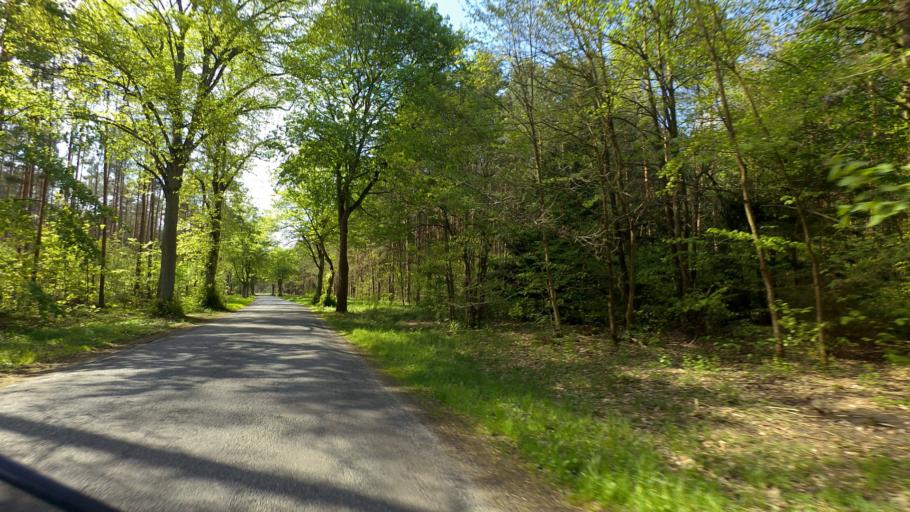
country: DE
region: Brandenburg
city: Templin
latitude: 52.9994
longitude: 13.5011
